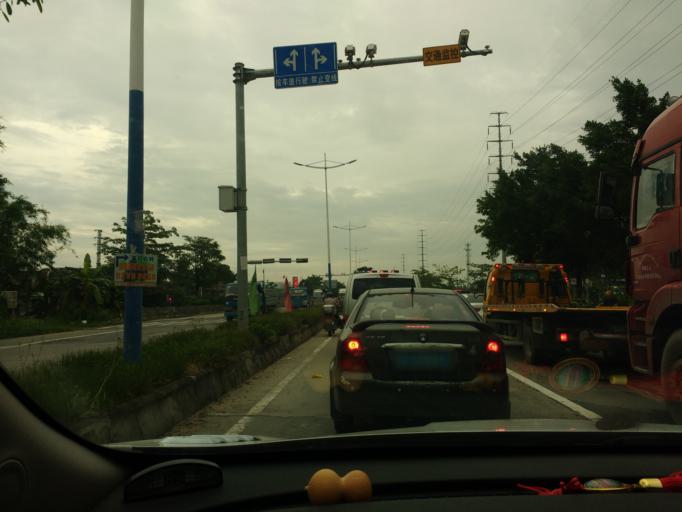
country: CN
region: Guangdong
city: Lile
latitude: 22.5195
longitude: 113.0852
